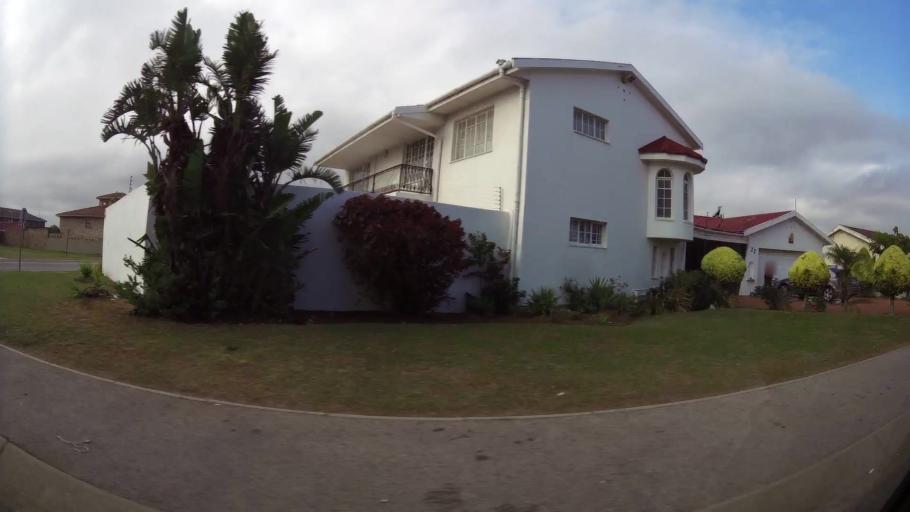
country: ZA
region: Eastern Cape
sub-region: Nelson Mandela Bay Metropolitan Municipality
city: Port Elizabeth
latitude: -33.9197
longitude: 25.5357
